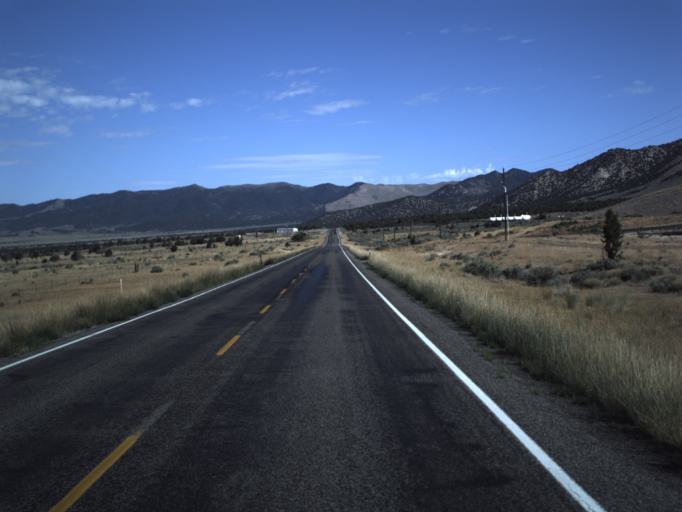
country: US
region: Utah
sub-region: Juab County
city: Mona
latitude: 39.9099
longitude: -112.1408
